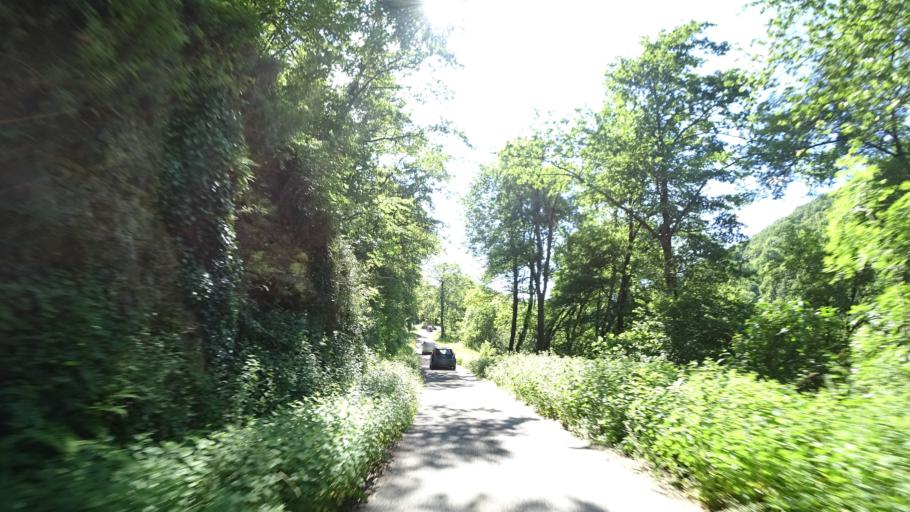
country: FR
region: Midi-Pyrenees
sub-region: Departement de l'Aveyron
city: Colombies
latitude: 44.3772
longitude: 2.3176
